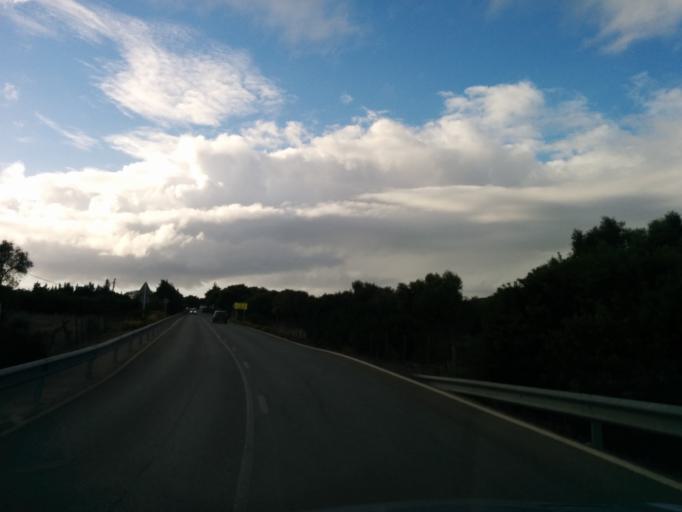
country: ES
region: Andalusia
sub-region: Provincia de Cadiz
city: Vejer de la Frontera
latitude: 36.1976
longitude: -6.0307
